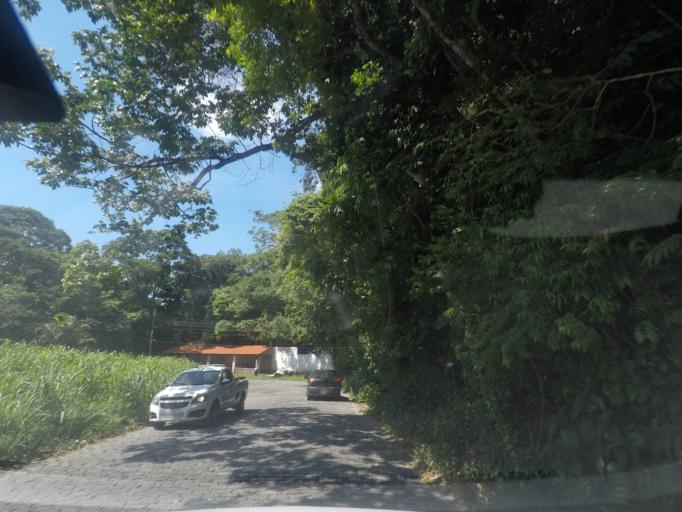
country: BR
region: Rio de Janeiro
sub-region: Petropolis
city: Petropolis
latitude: -22.5475
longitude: -43.1832
